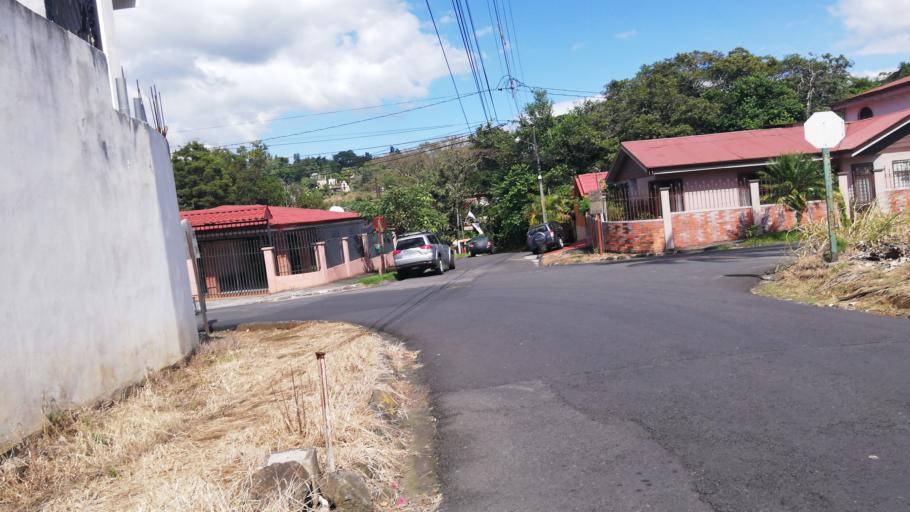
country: CR
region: Alajuela
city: San Juan
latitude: 10.0797
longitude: -84.3113
